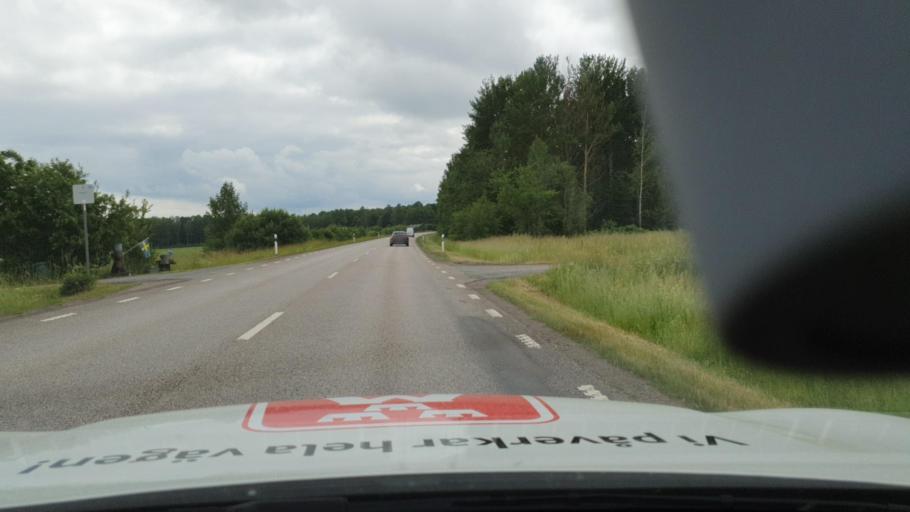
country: SE
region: Vaestra Goetaland
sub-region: Hjo Kommun
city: Hjo
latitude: 58.2416
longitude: 14.2281
